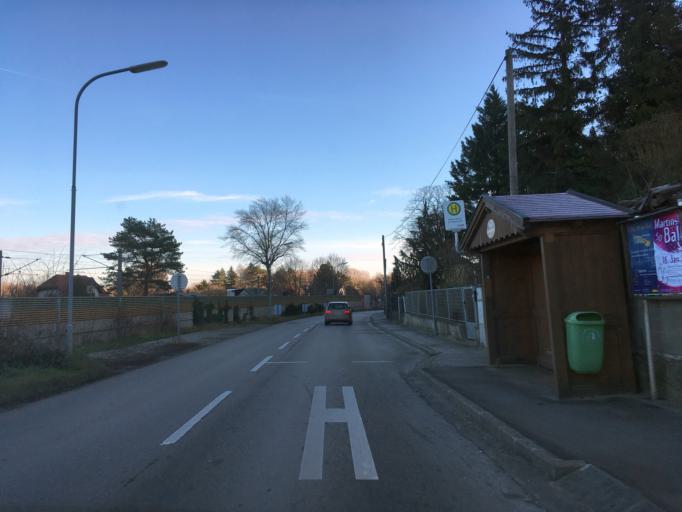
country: AT
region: Lower Austria
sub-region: Politischer Bezirk Korneuburg
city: Leobendorf
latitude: 48.3477
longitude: 16.2849
